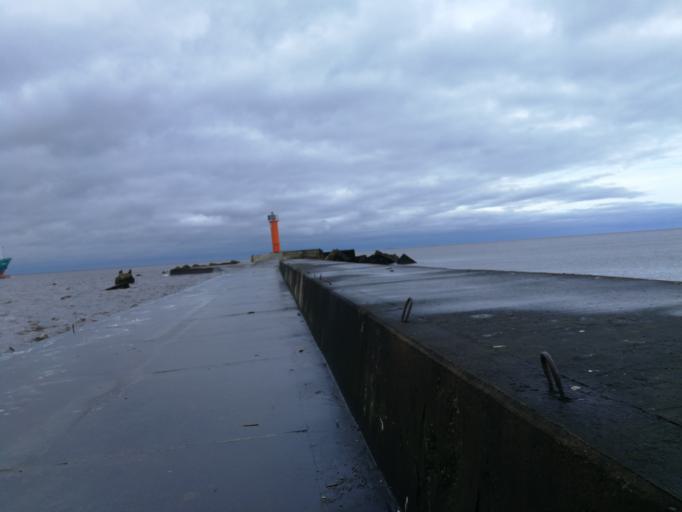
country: LV
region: Riga
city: Daugavgriva
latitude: 57.0680
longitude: 24.0167
